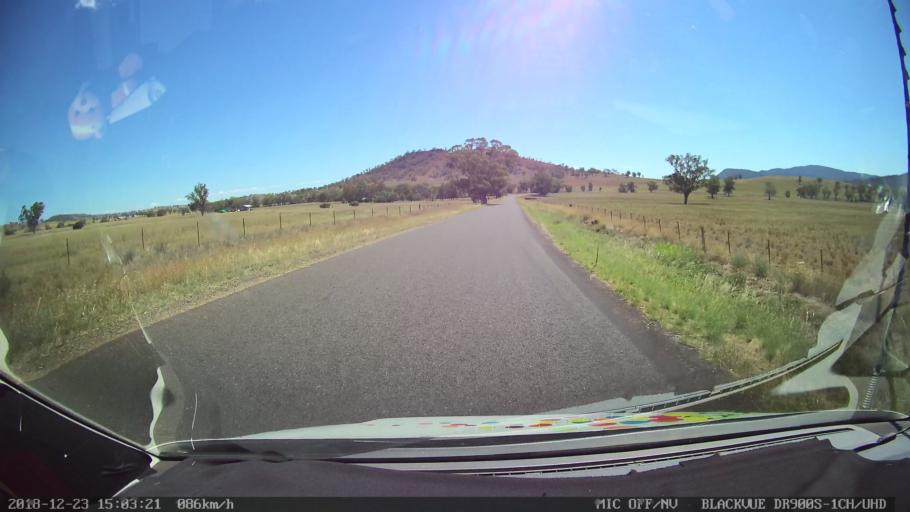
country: AU
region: New South Wales
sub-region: Tamworth Municipality
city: Manilla
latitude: -30.7378
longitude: 150.7659
